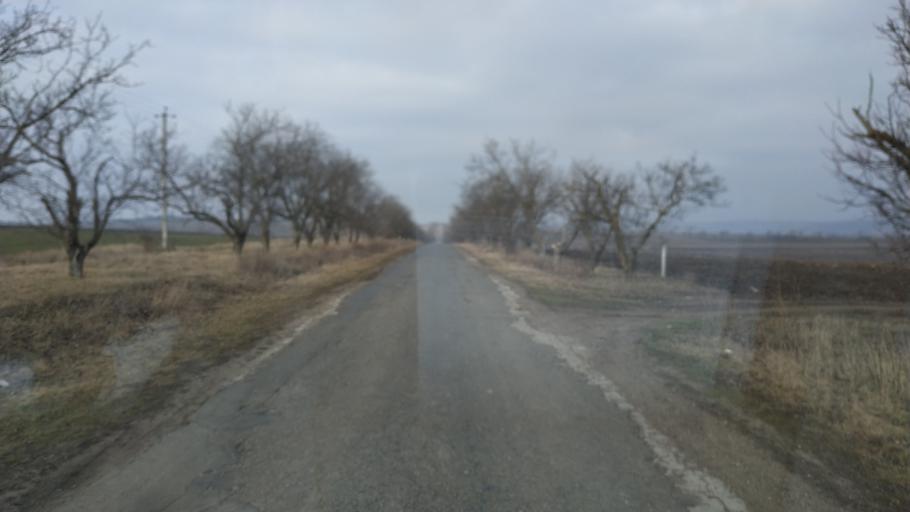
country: MD
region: Hincesti
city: Dancu
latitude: 46.8680
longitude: 28.2933
